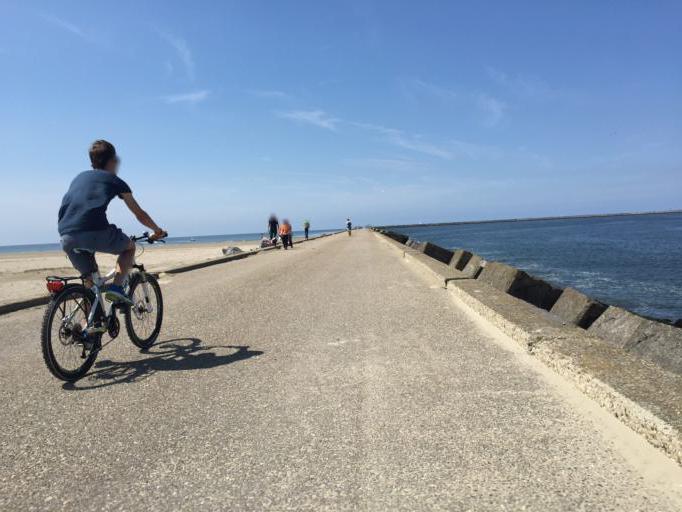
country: NL
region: North Holland
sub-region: Gemeente Zandvoort
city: Zandvoort
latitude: 52.4613
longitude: 4.5538
